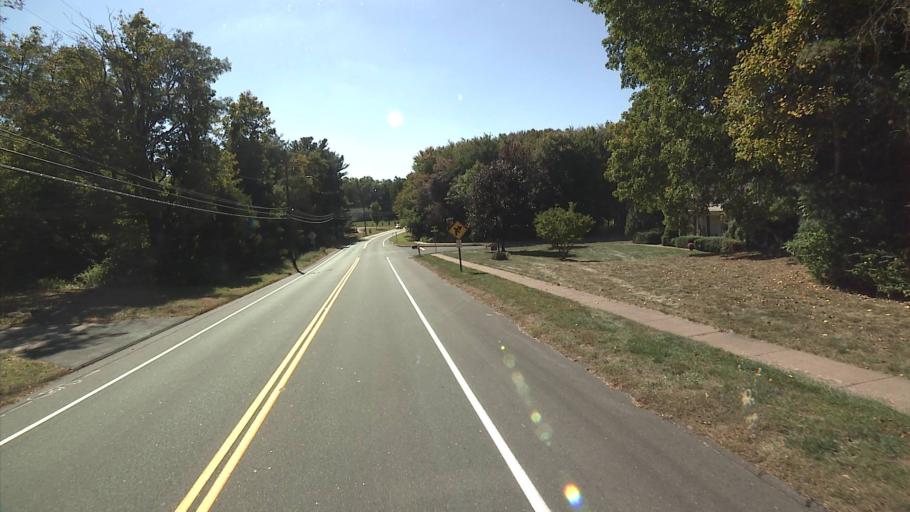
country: US
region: Connecticut
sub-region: Hartford County
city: Manchester
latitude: 41.7416
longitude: -72.5172
